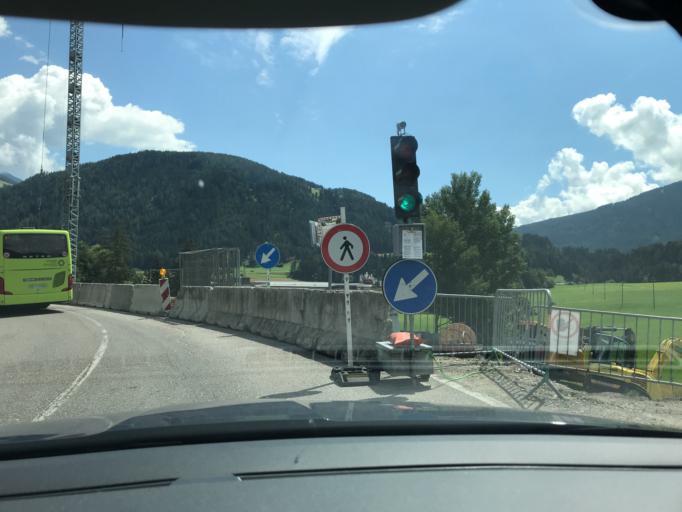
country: IT
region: Trentino-Alto Adige
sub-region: Bolzano
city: Valdaora di Mezzo
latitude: 46.7711
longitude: 12.0320
